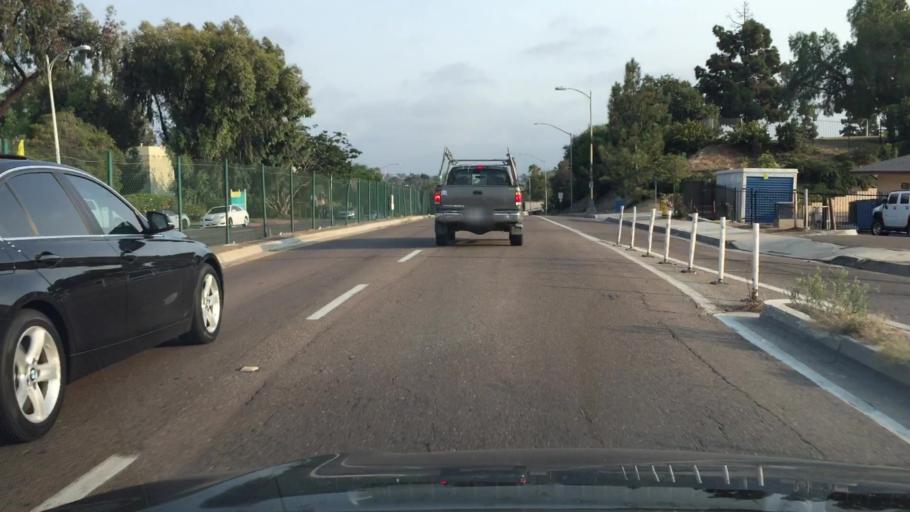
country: US
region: California
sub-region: San Diego County
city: Lemon Grove
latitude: 32.7520
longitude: -117.0795
